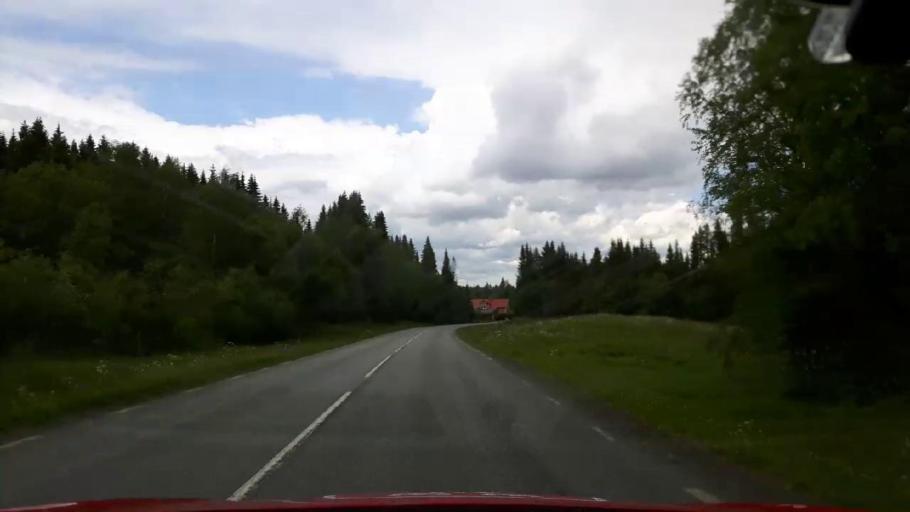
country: SE
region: Jaemtland
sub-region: Krokoms Kommun
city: Krokom
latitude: 63.4985
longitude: 14.2133
